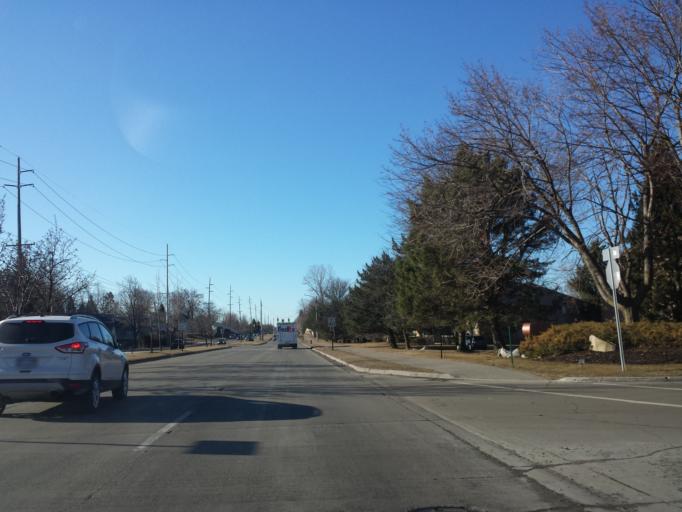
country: US
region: Michigan
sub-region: Oakland County
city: Rochester Hills
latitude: 42.6751
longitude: -83.1535
